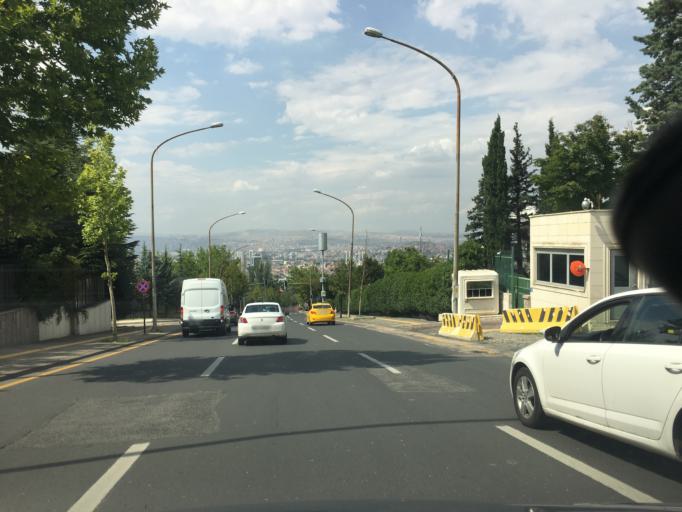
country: TR
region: Ankara
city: Cankaya
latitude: 39.8920
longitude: 32.8627
